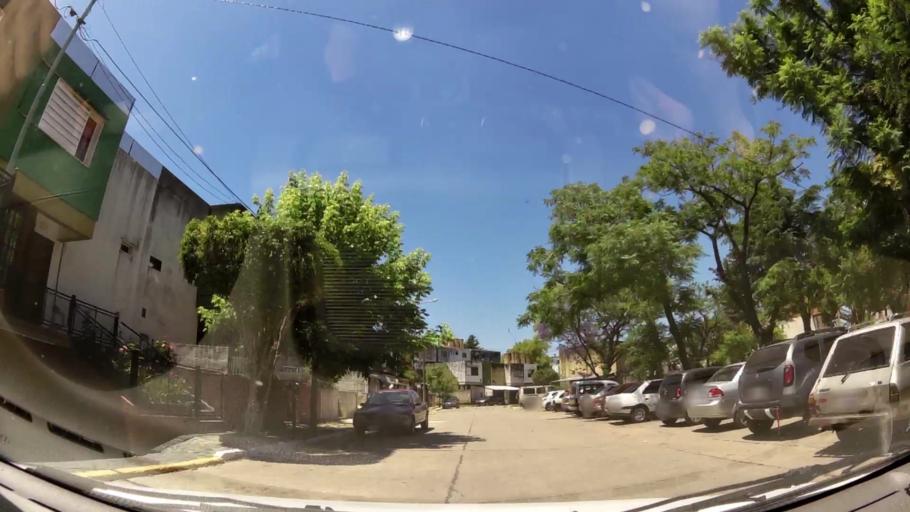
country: AR
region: Buenos Aires
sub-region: Partido de Merlo
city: Merlo
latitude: -34.6519
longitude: -58.7096
